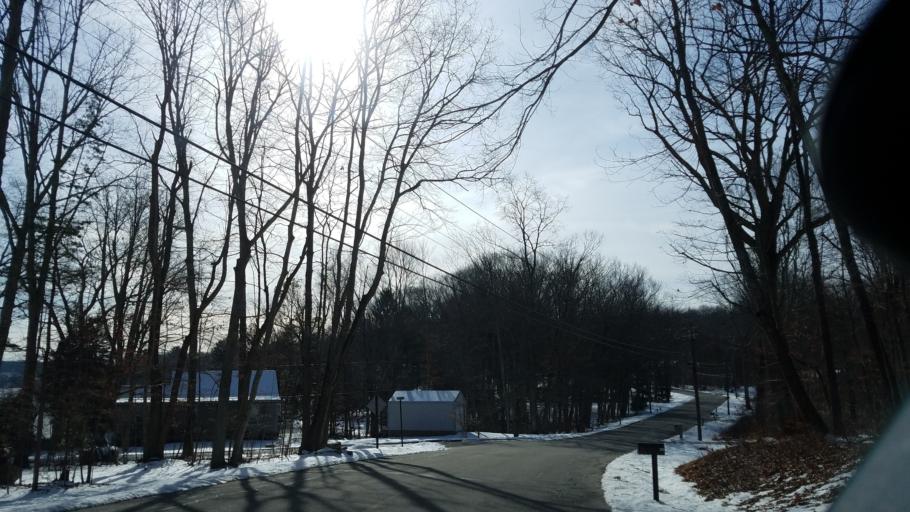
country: US
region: Connecticut
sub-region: Tolland County
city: Coventry Lake
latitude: 41.7233
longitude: -72.3616
